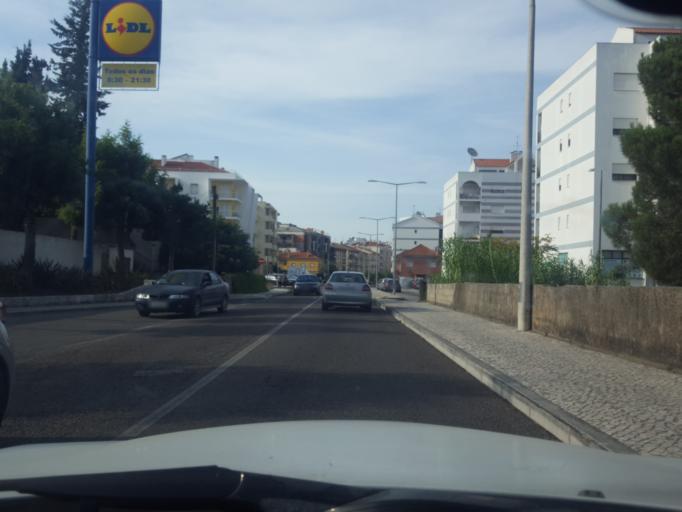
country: PT
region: Leiria
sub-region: Leiria
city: Leiria
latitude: 39.7314
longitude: -8.7984
